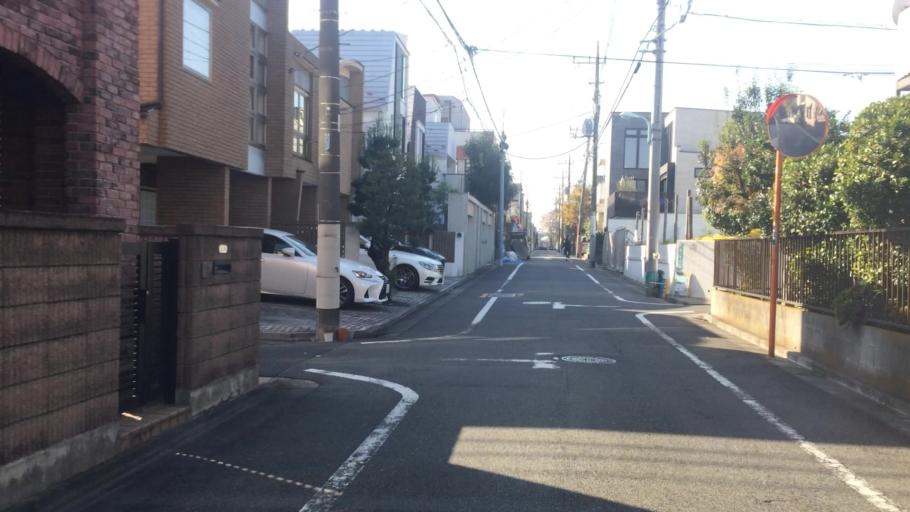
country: JP
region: Tokyo
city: Tokyo
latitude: 35.6175
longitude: 139.6681
